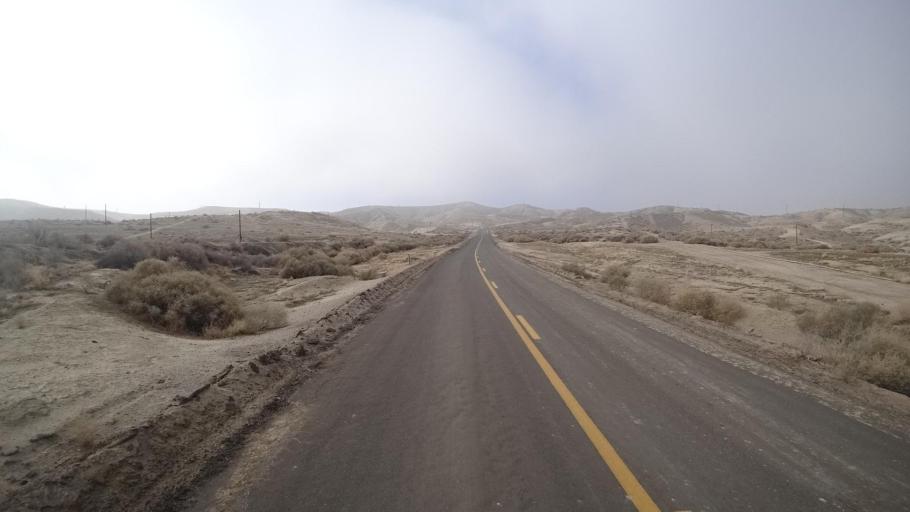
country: US
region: California
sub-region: Kern County
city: Ford City
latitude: 35.1655
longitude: -119.3981
